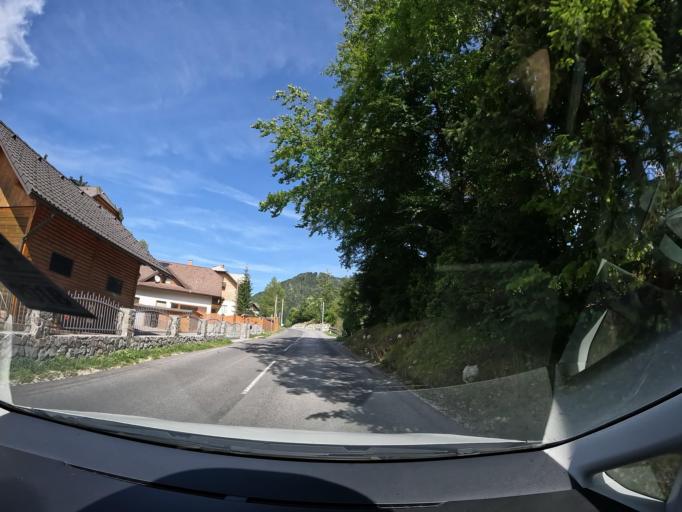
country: AT
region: Carinthia
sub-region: Politischer Bezirk Klagenfurt Land
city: Moosburg
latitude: 46.6672
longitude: 14.1279
